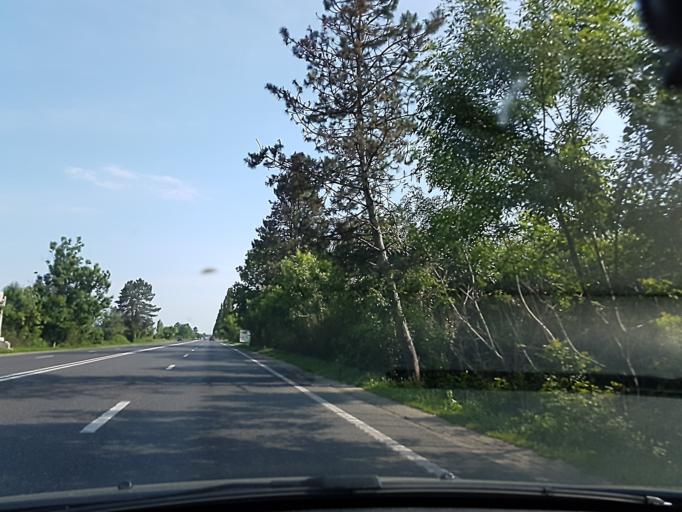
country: RO
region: Prahova
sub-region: Comuna Gorgota
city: Potigrafu
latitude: 44.7640
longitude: 26.1038
